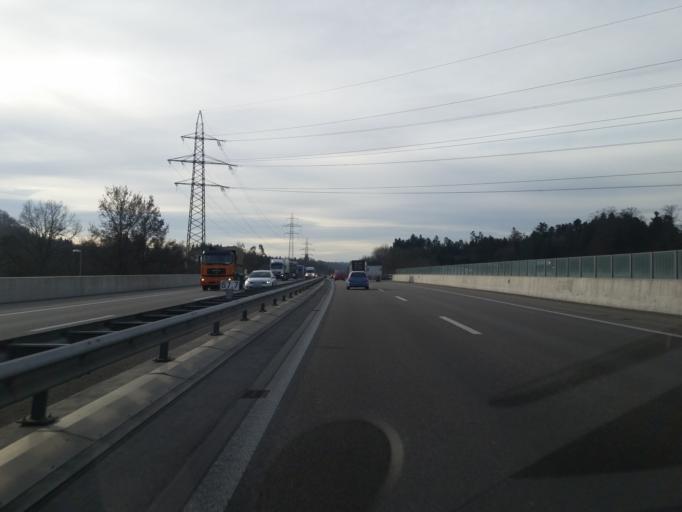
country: CH
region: Aargau
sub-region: Bezirk Lenzburg
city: Othmarsingen
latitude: 47.4174
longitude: 8.2232
